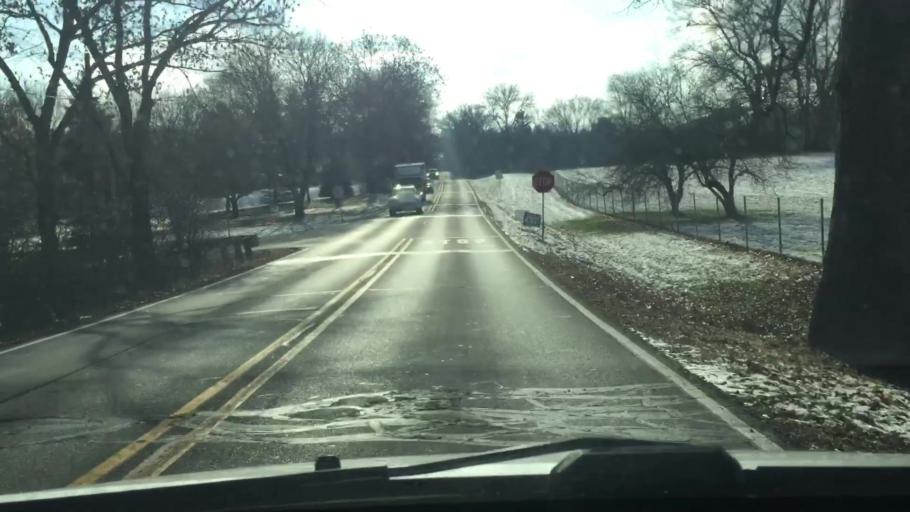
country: US
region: Wisconsin
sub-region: Waukesha County
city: Waukesha
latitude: 42.9840
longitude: -88.2871
